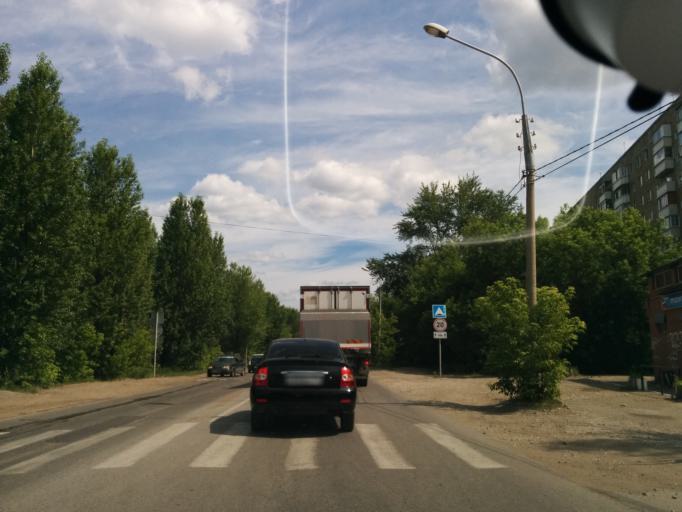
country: RU
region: Perm
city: Overyata
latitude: 58.0140
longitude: 55.9567
